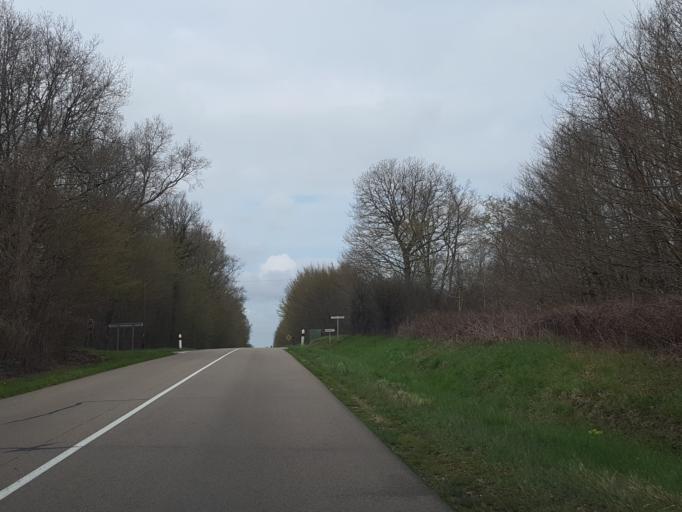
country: FR
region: Centre
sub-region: Departement du Loiret
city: Sainte-Genevieve-des-Bois
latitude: 47.8245
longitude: 2.8139
